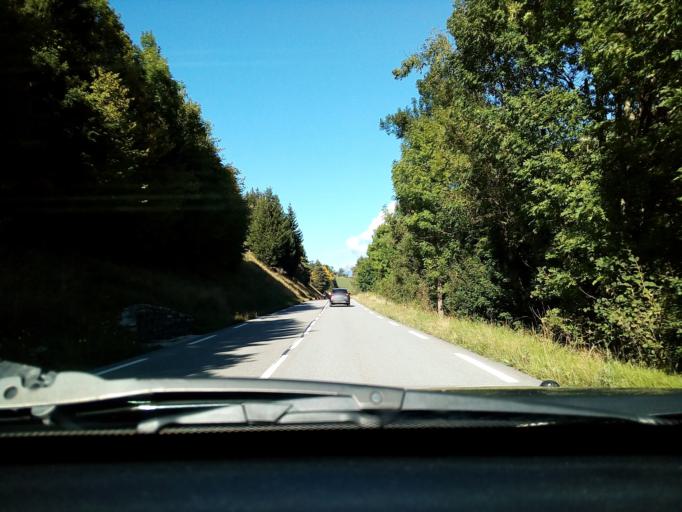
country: FR
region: Rhone-Alpes
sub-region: Departement de l'Isere
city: Lans-en-Vercors
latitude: 45.1675
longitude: 5.6121
